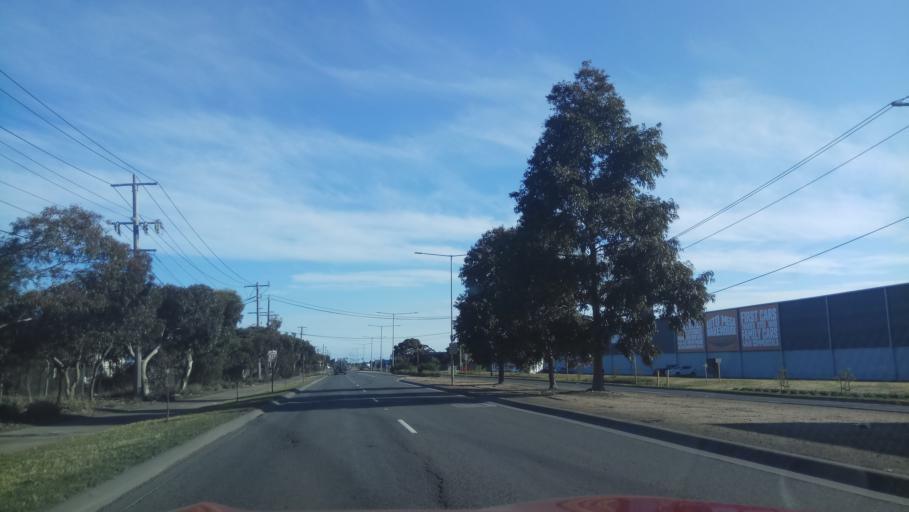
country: AU
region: Victoria
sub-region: Hobsons Bay
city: Altona North
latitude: -37.8350
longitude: 144.8262
